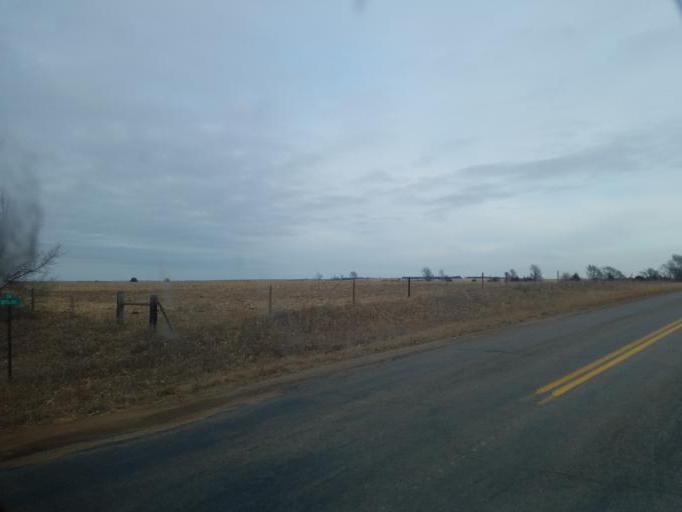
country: US
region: Nebraska
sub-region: Holt County
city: O'Neill
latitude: 42.4659
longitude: -98.3055
